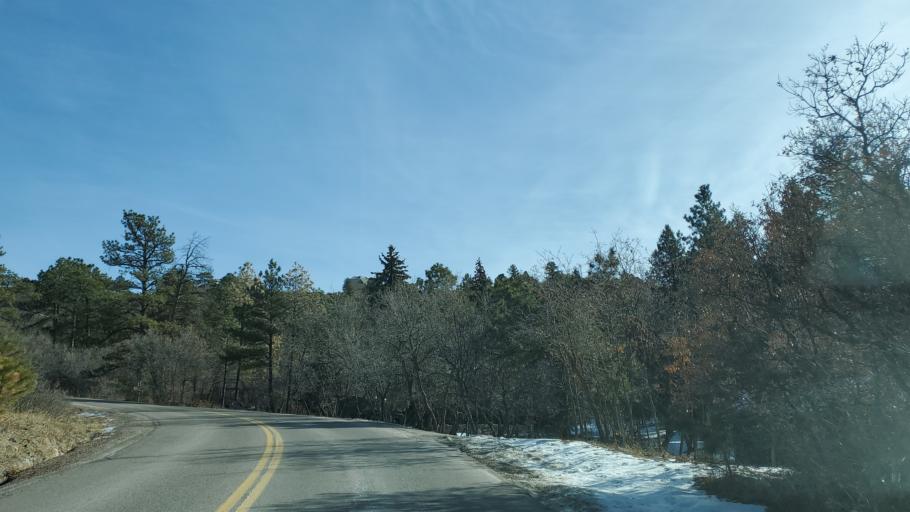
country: US
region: Colorado
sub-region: Douglas County
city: Castle Pines
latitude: 39.4386
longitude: -104.8742
